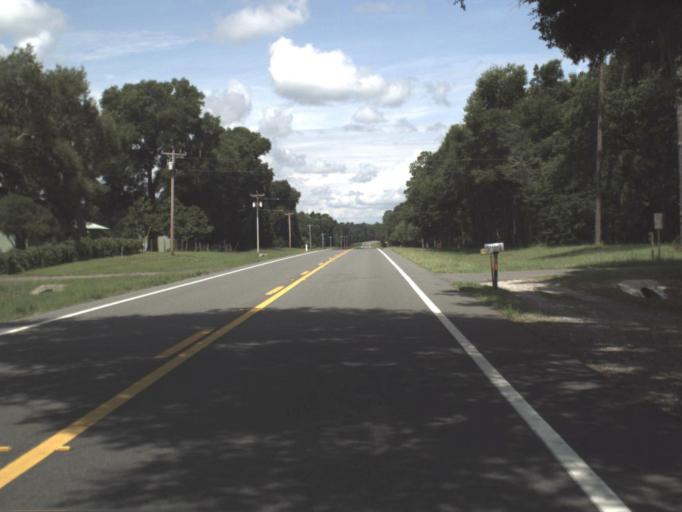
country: US
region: Florida
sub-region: Alachua County
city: Alachua
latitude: 29.8400
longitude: -82.3706
